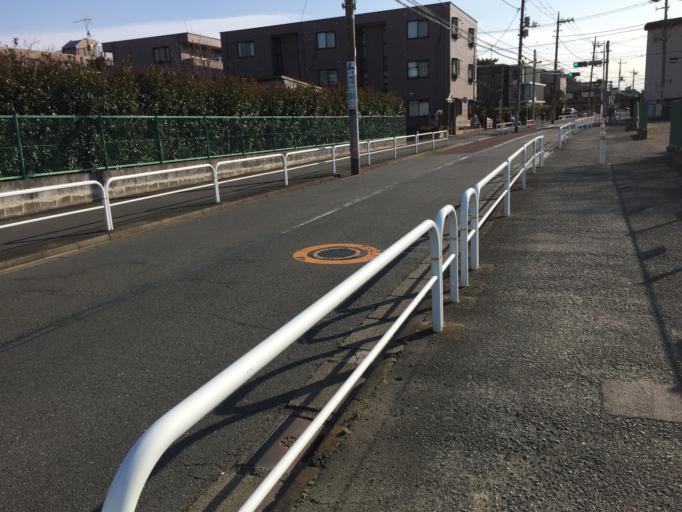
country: JP
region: Tokyo
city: Mitaka-shi
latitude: 35.6650
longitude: 139.6079
